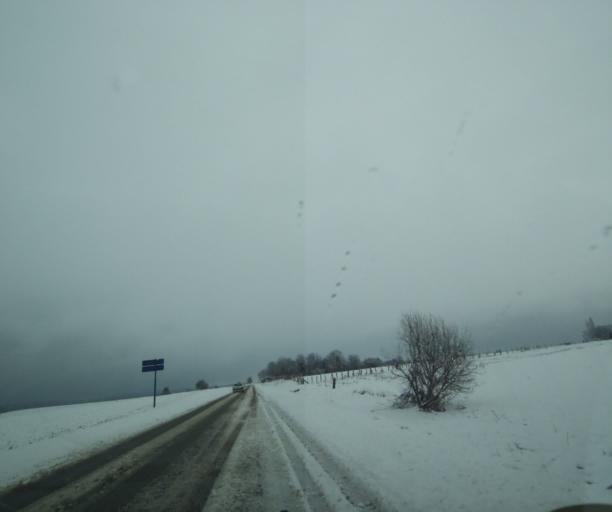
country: FR
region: Champagne-Ardenne
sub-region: Departement de la Haute-Marne
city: Montier-en-Der
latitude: 48.5232
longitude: 4.8063
